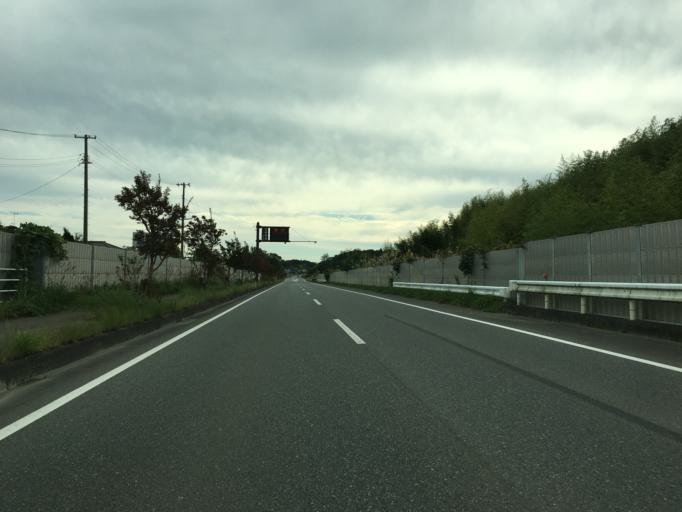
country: JP
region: Miyagi
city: Marumori
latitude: 37.8248
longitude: 140.9411
